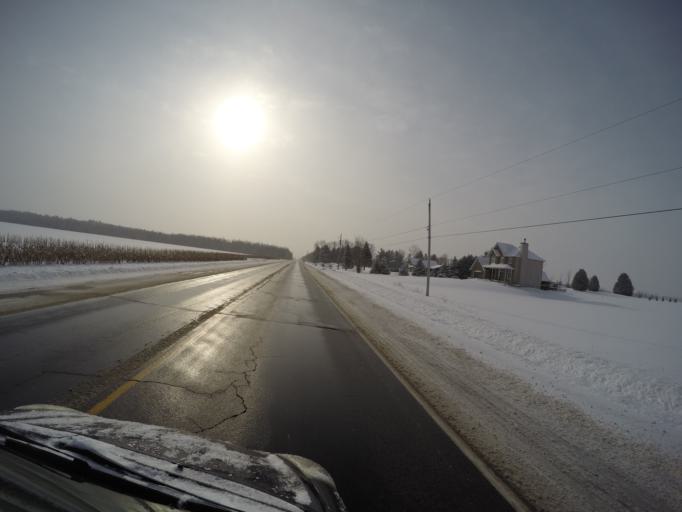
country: CA
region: Ontario
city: Clarence-Rockland
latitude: 45.4386
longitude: -75.4172
